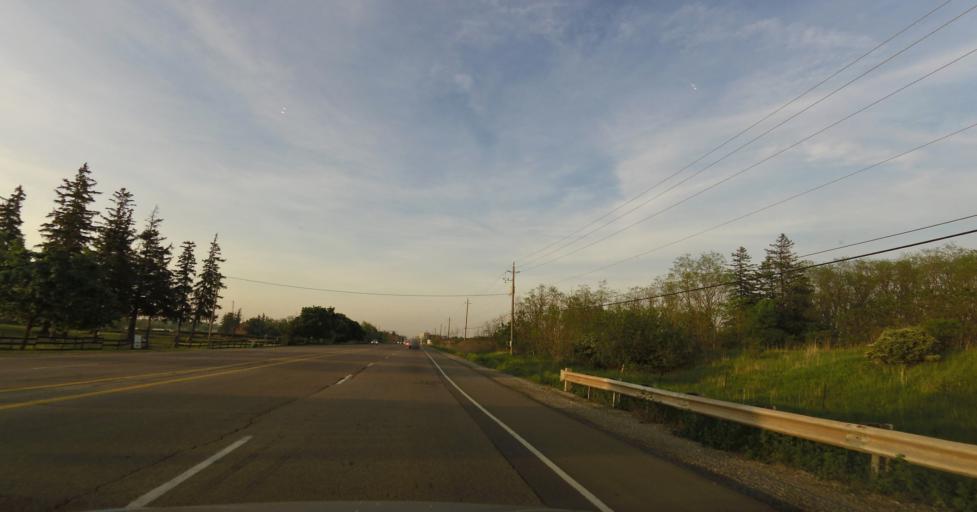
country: CA
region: Ontario
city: Burlington
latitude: 43.4228
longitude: -79.7900
